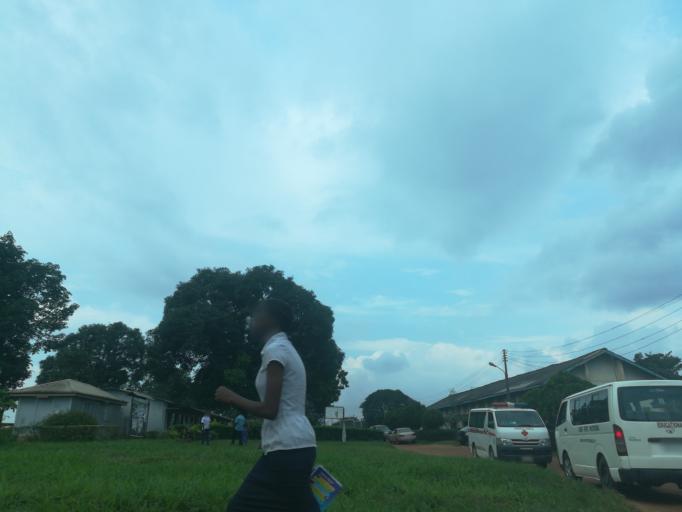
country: NG
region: Lagos
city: Ikorodu
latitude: 6.6449
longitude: 3.5223
